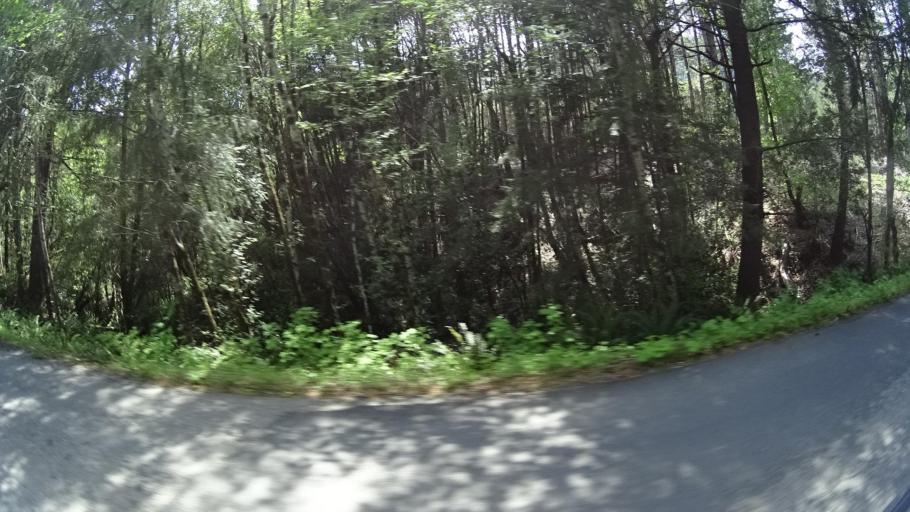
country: US
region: California
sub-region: Humboldt County
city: Redway
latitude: 40.3748
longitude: -123.7397
